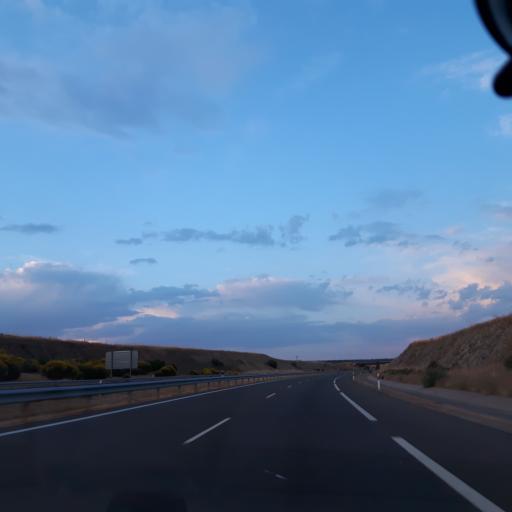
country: ES
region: Castille and Leon
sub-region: Provincia de Salamanca
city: Mozarbez
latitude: 40.8600
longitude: -5.6426
